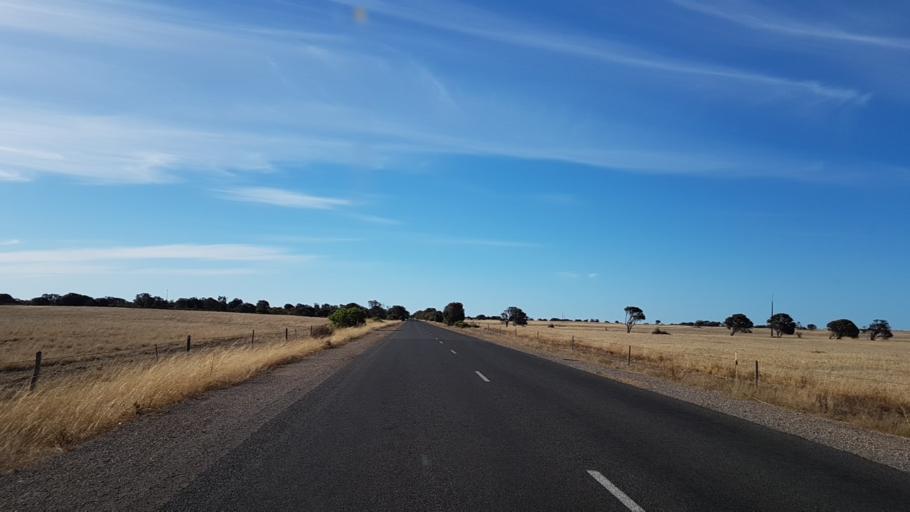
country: AU
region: South Australia
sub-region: Yorke Peninsula
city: Honiton
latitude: -34.9395
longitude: 137.0921
